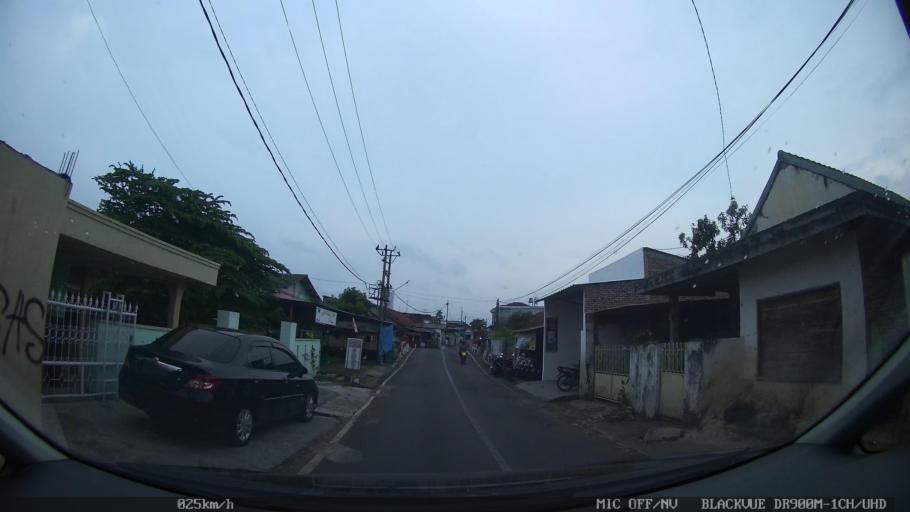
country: ID
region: Lampung
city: Kedaton
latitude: -5.4004
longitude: 105.2640
